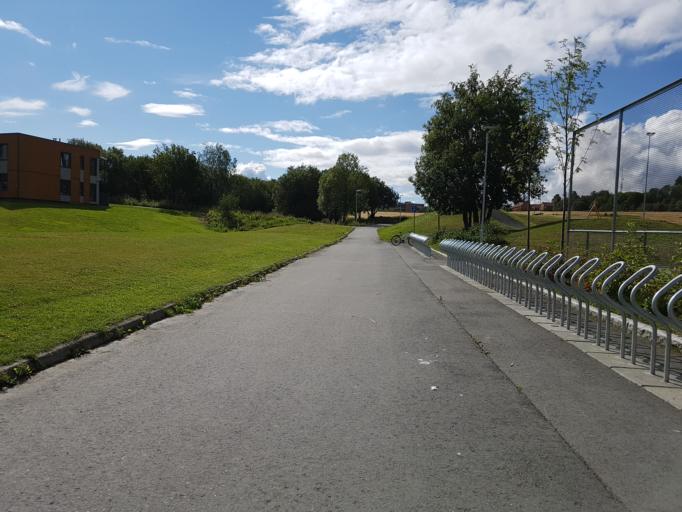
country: NO
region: Sor-Trondelag
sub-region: Trondheim
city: Trondheim
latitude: 63.4176
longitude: 10.4800
